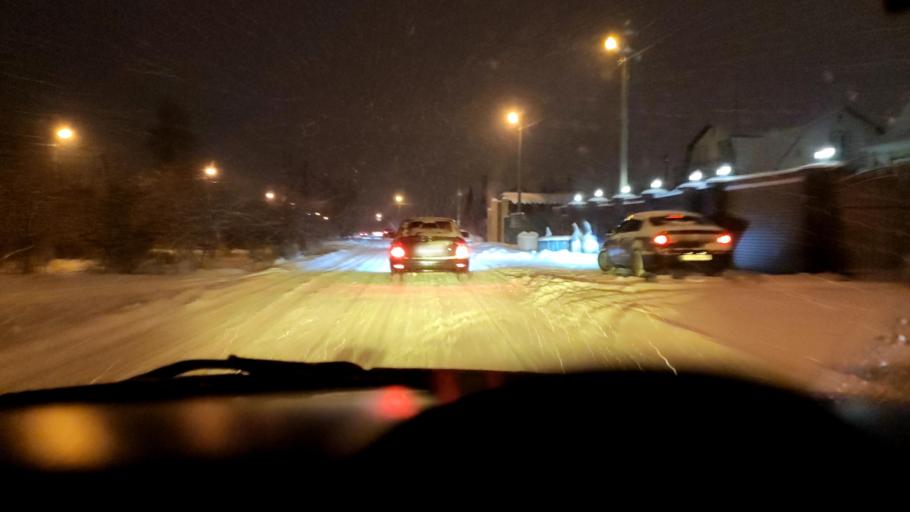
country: RU
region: Voronezj
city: Pridonskoy
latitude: 51.6737
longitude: 39.0770
